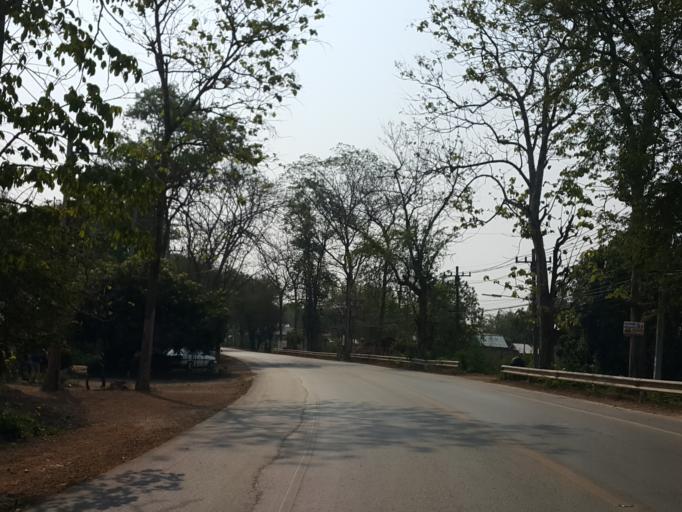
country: TH
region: Sukhothai
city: Ban Na
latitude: 17.0217
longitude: 99.6881
